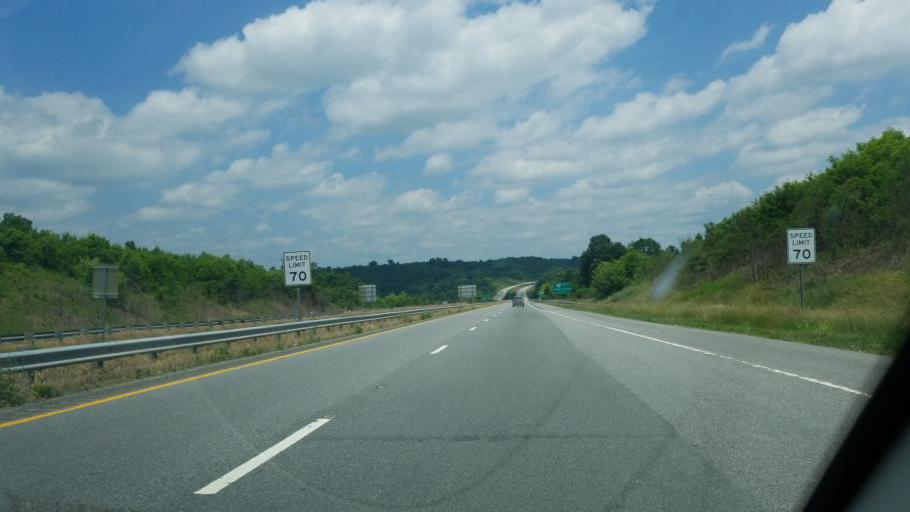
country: US
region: Virginia
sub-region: Amherst County
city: Madison Heights
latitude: 37.3924
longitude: -79.0890
